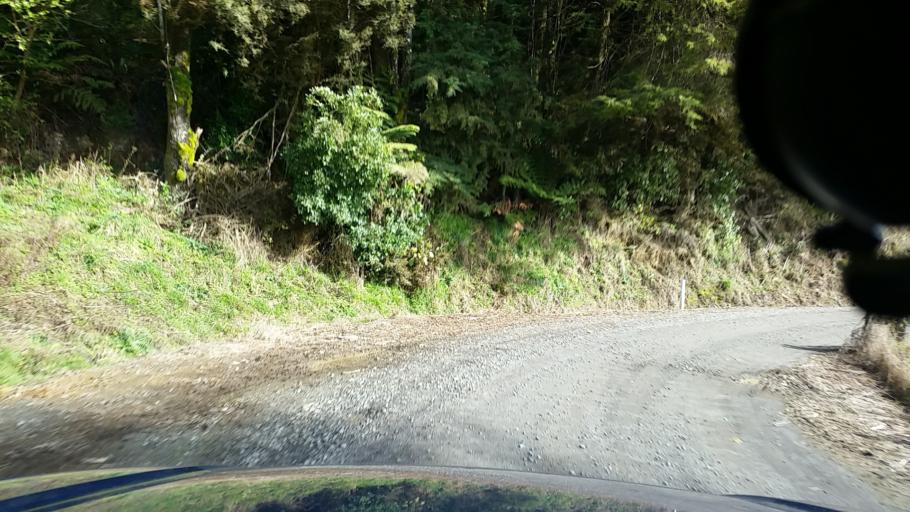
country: NZ
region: Taranaki
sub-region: New Plymouth District
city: Waitara
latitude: -39.0322
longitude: 174.7918
